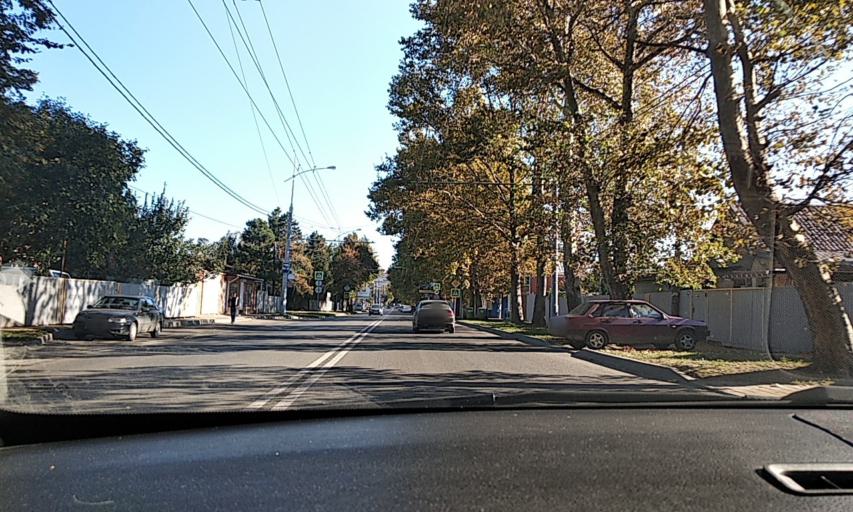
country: RU
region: Krasnodarskiy
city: Pashkovskiy
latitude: 45.0262
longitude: 39.1167
